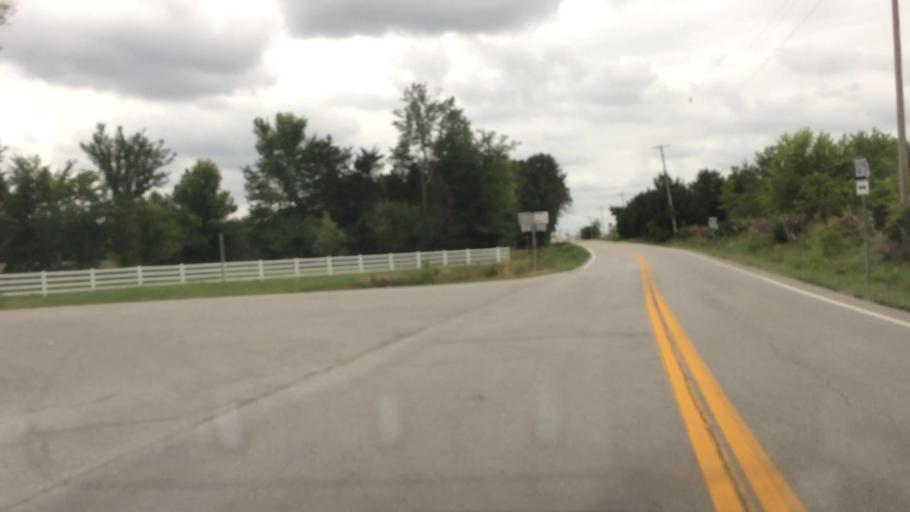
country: US
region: Missouri
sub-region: Greene County
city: Strafford
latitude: 37.2813
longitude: -93.1132
